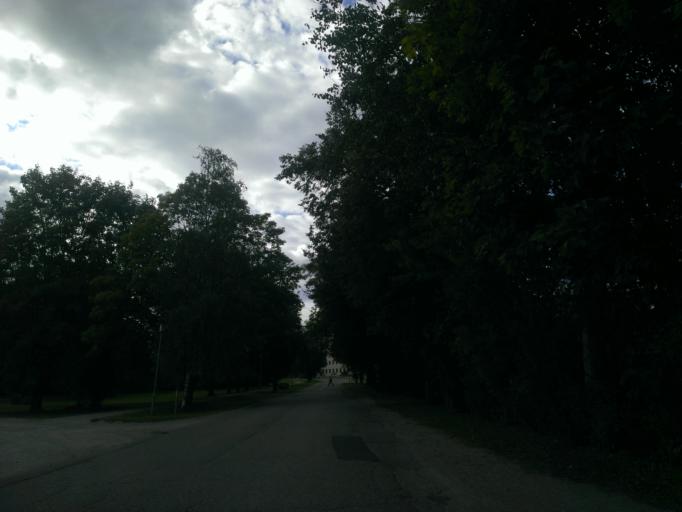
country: LV
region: Sigulda
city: Sigulda
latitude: 57.1531
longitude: 24.8862
